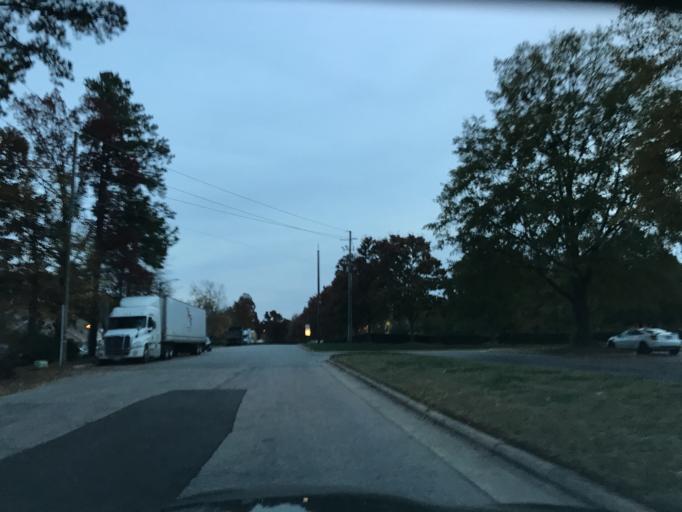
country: US
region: North Carolina
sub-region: Wake County
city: West Raleigh
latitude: 35.8469
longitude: -78.6121
